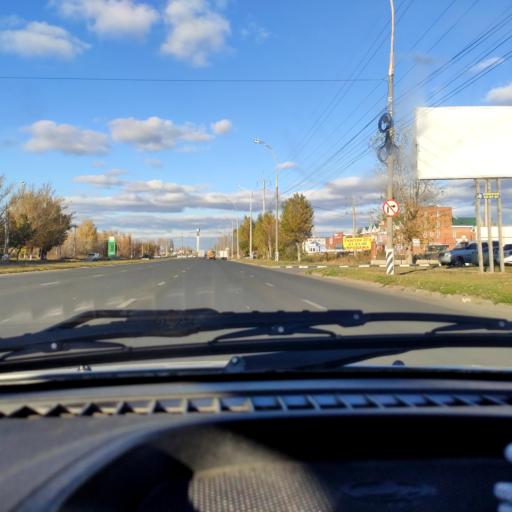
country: RU
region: Samara
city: Tol'yatti
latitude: 53.5478
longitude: 49.2865
